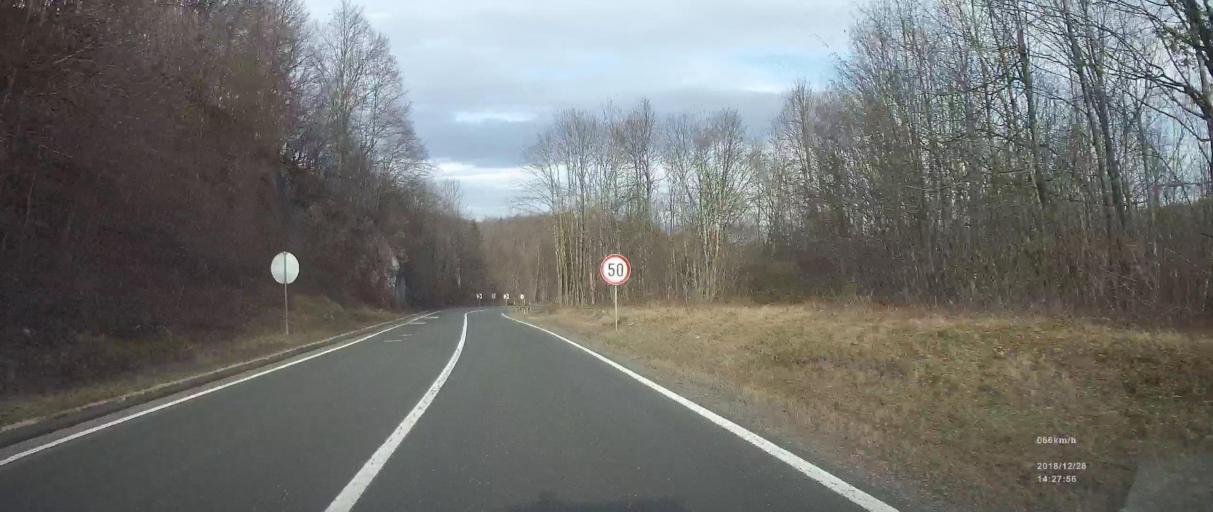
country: HR
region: Primorsko-Goranska
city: Vrbovsko
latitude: 45.4060
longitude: 15.1096
